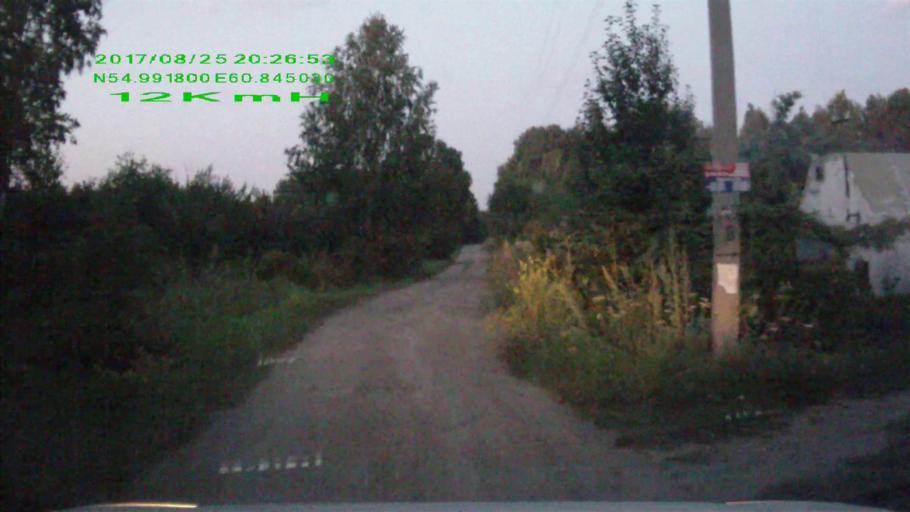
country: RU
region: Chelyabinsk
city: Timiryazevskiy
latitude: 54.9918
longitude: 60.8451
